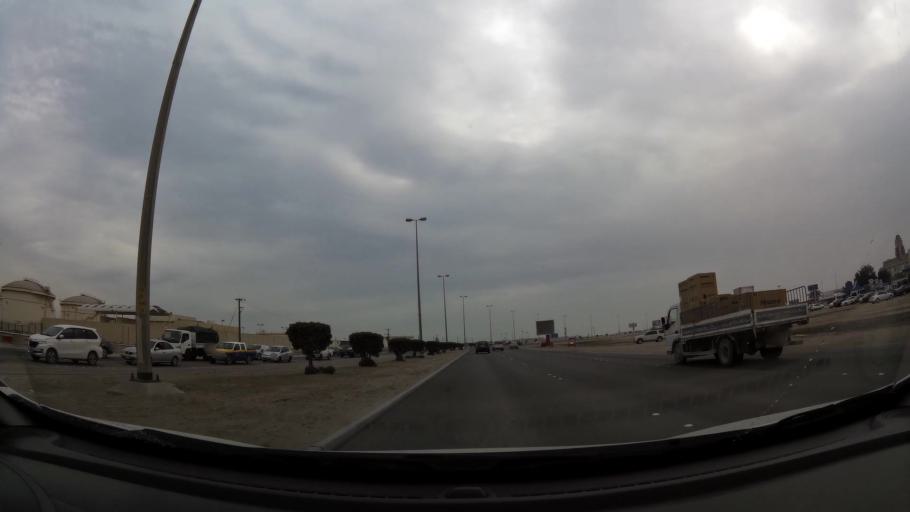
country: BH
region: Northern
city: Sitrah
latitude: 26.1469
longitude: 50.6188
